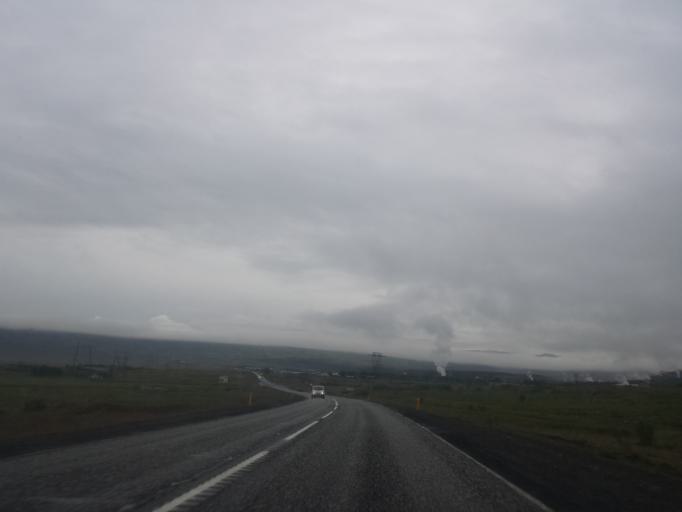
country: IS
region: South
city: Hveragerdi
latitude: 63.9855
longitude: -21.1598
